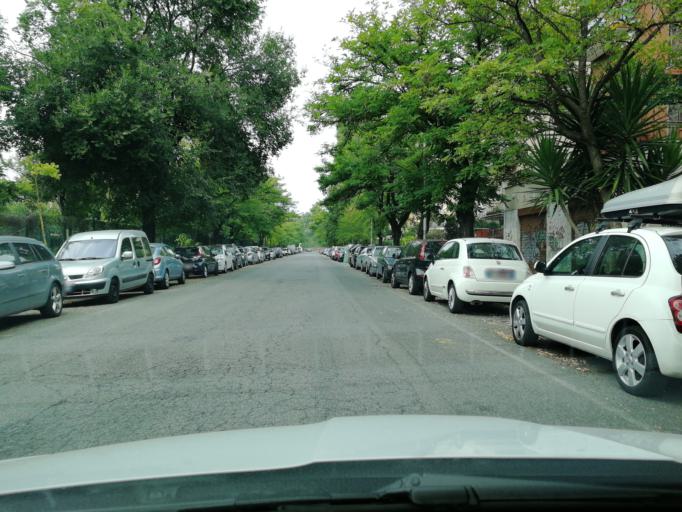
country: IT
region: Latium
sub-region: Citta metropolitana di Roma Capitale
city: Rome
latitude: 41.8621
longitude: 12.5460
